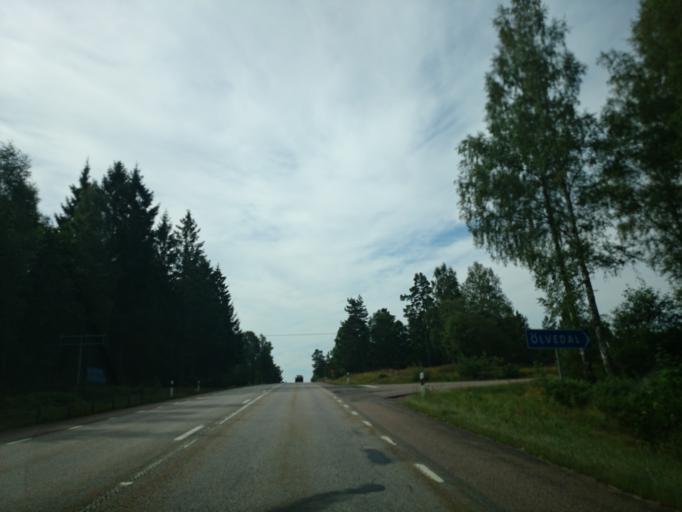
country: SE
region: Kalmar
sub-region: Oskarshamns Kommun
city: Oskarshamn
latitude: 57.4758
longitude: 16.5175
